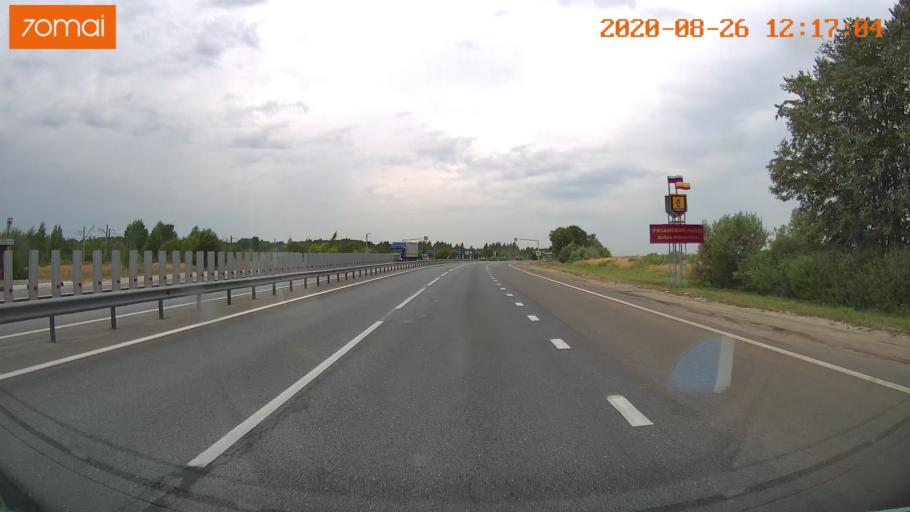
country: RU
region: Rjazan
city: Murmino
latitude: 54.4561
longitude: 40.0329
